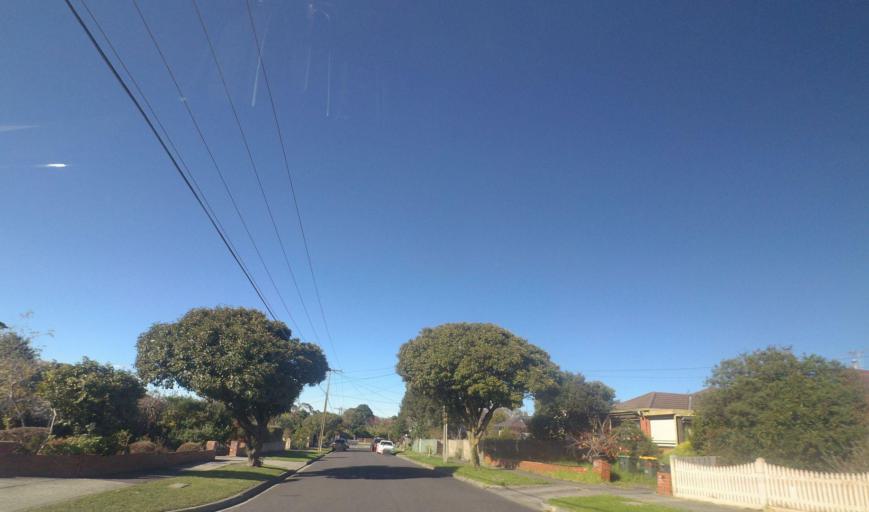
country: AU
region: Victoria
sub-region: Whitehorse
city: Blackburn North
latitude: -37.8062
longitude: 145.1398
